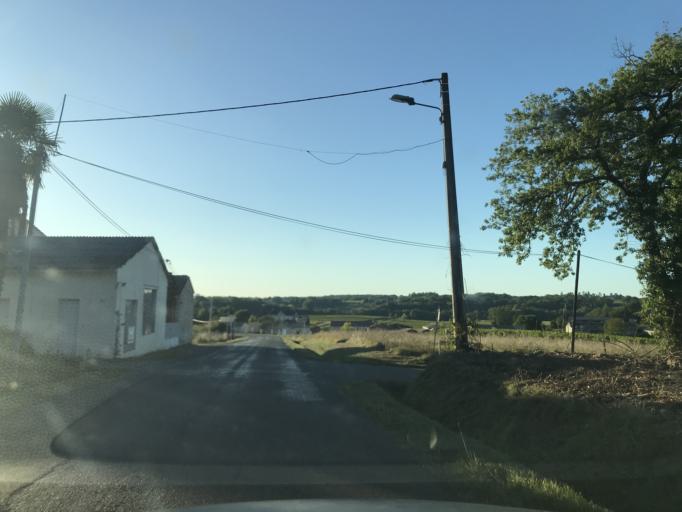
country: FR
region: Aquitaine
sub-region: Departement de la Gironde
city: Lussac
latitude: 44.8987
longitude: -0.0664
